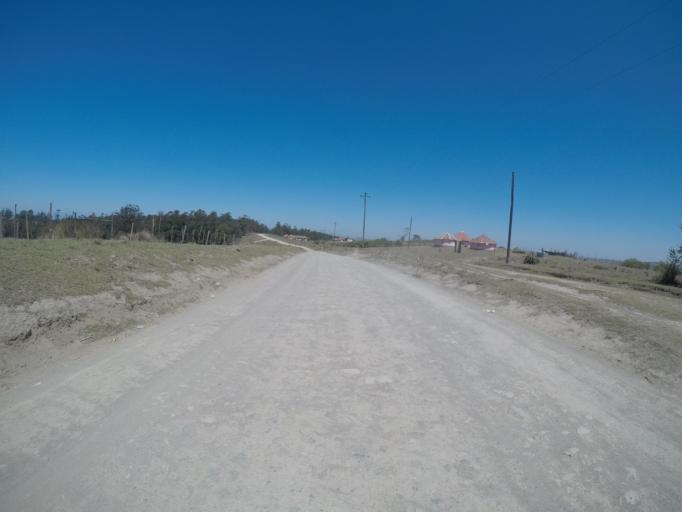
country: ZA
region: Eastern Cape
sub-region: OR Tambo District Municipality
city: Libode
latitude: -31.9456
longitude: 29.0259
